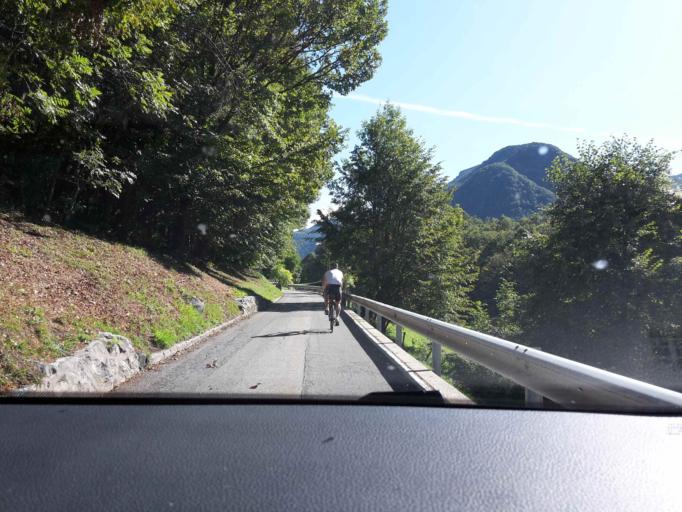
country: CH
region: Ticino
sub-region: Bellinzona District
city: Bellinzona
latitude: 46.1683
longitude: 9.0465
